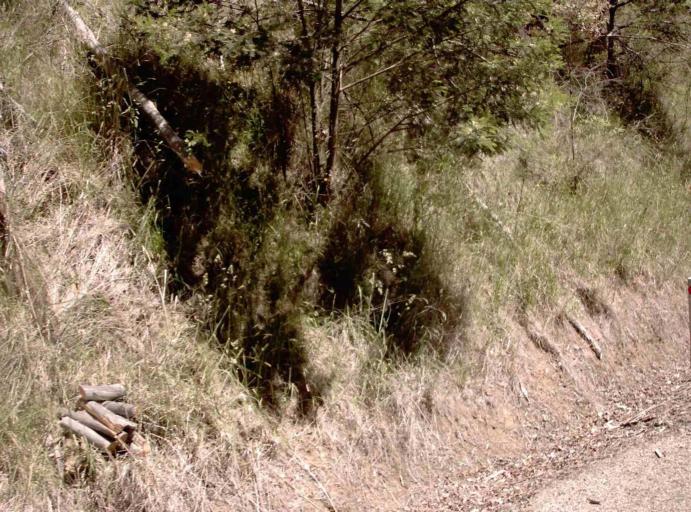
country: AU
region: Victoria
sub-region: East Gippsland
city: Lakes Entrance
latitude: -37.2411
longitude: 148.2556
